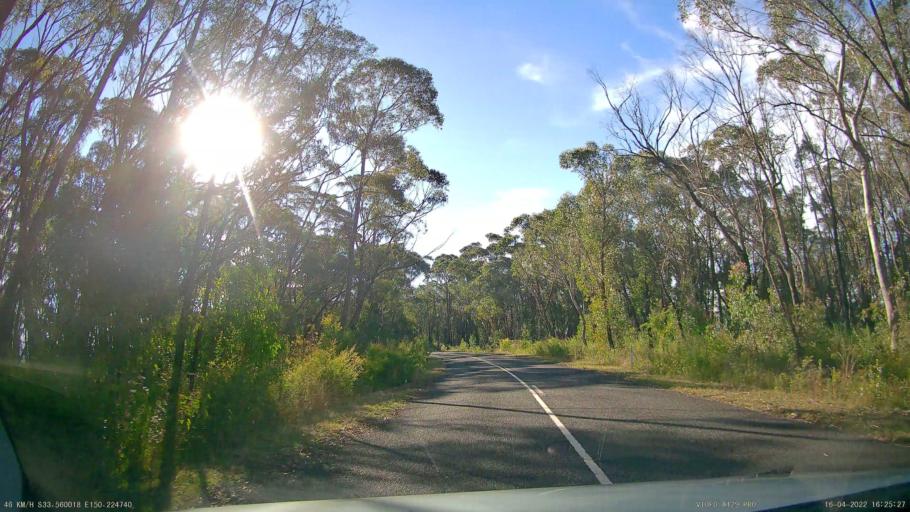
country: AU
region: New South Wales
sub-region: Blue Mountains Municipality
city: Blackheath
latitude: -33.5598
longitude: 150.2246
